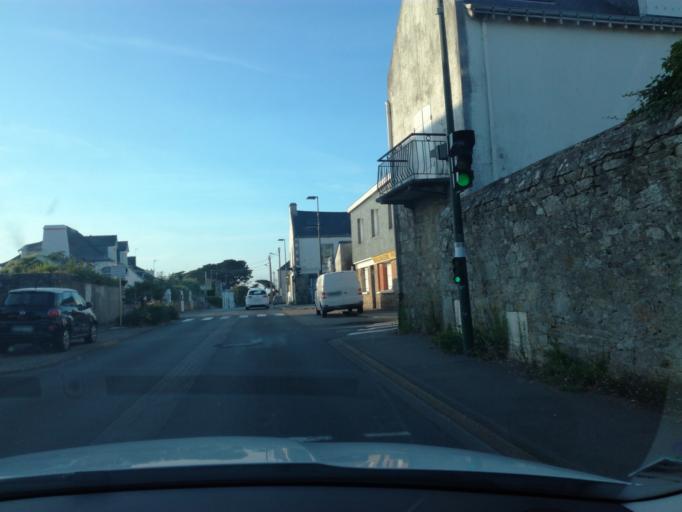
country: FR
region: Brittany
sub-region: Departement du Morbihan
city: Saint-Pierre-Quiberon
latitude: 47.5362
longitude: -3.1350
